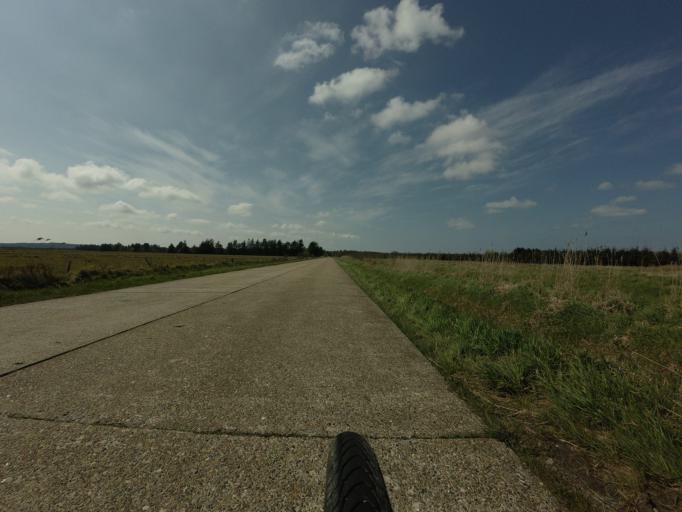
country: DK
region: North Denmark
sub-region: Jammerbugt Kommune
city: Brovst
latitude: 57.1644
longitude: 9.4989
